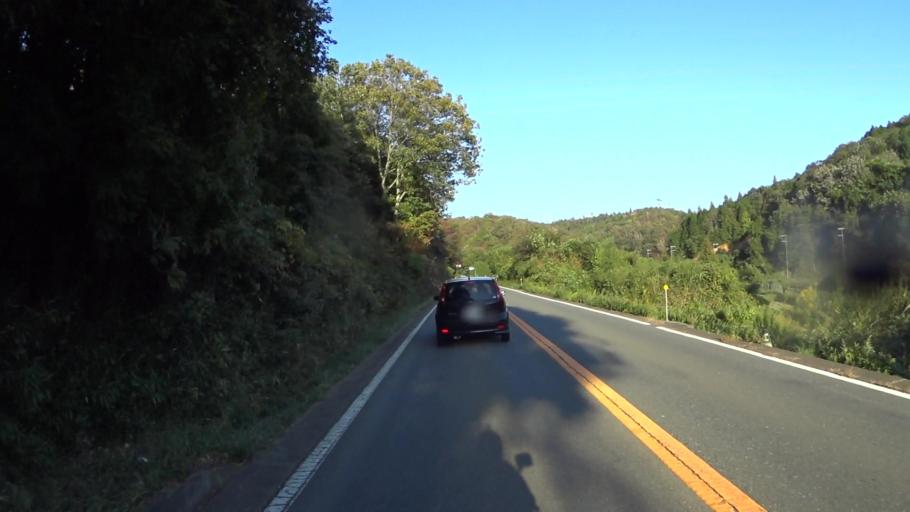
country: JP
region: Kyoto
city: Ayabe
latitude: 35.1886
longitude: 135.3296
